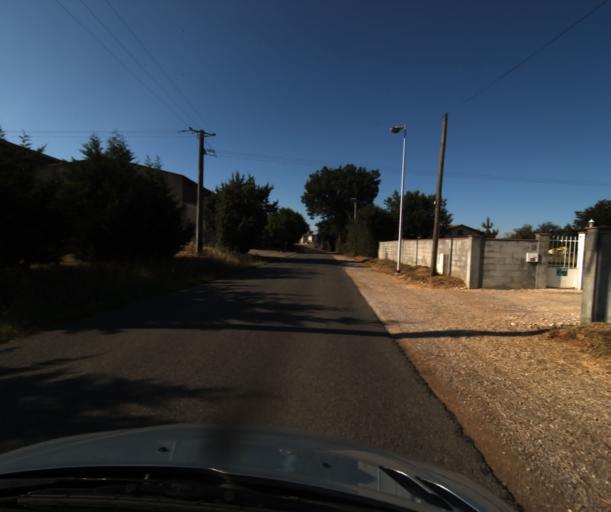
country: FR
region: Midi-Pyrenees
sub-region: Departement du Tarn-et-Garonne
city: Saint-Porquier
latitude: 44.0384
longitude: 1.2170
